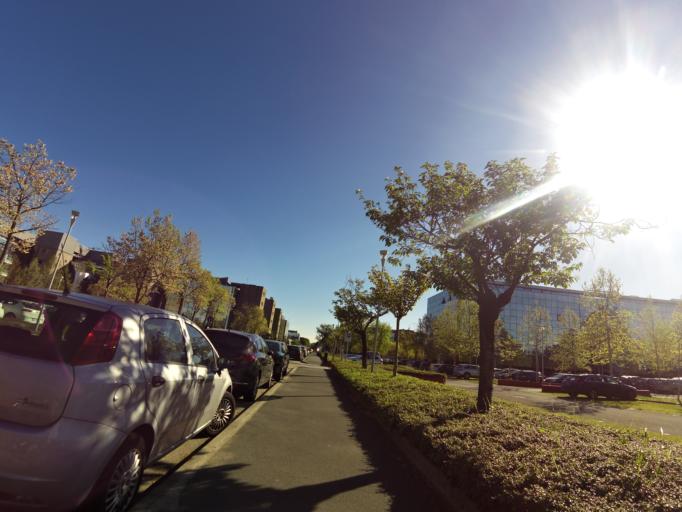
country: IT
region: Lombardy
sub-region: Citta metropolitana di Milano
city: Rozzano
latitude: 45.3992
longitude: 9.1504
